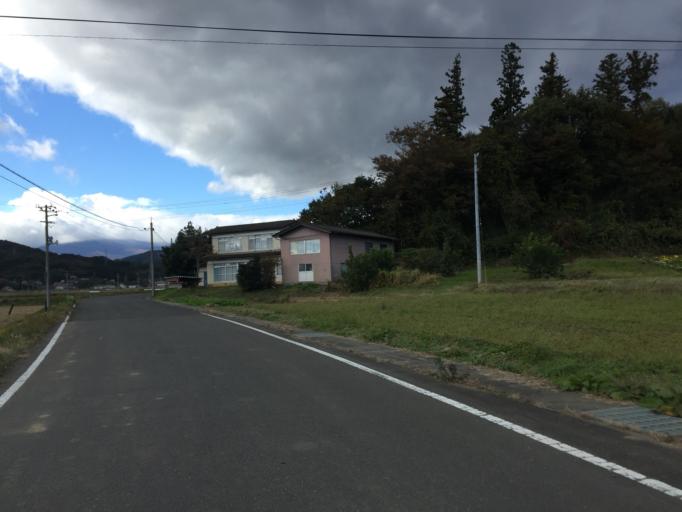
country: JP
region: Fukushima
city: Nihommatsu
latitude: 37.6616
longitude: 140.4343
